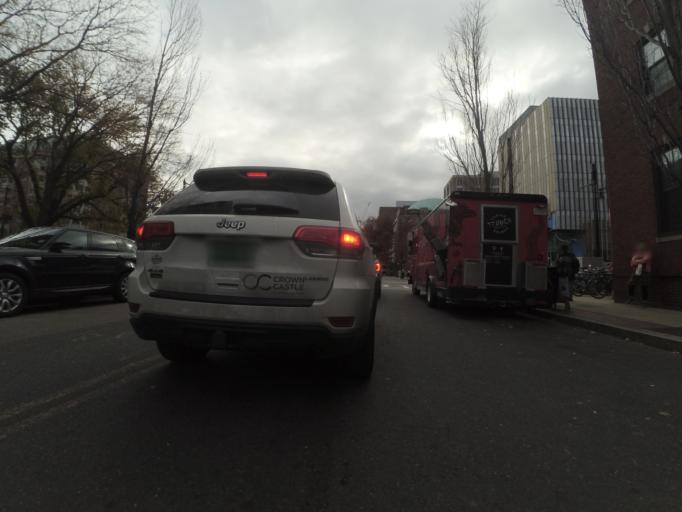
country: US
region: Massachusetts
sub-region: Middlesex County
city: Cambridge
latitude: 42.3496
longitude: -71.1004
